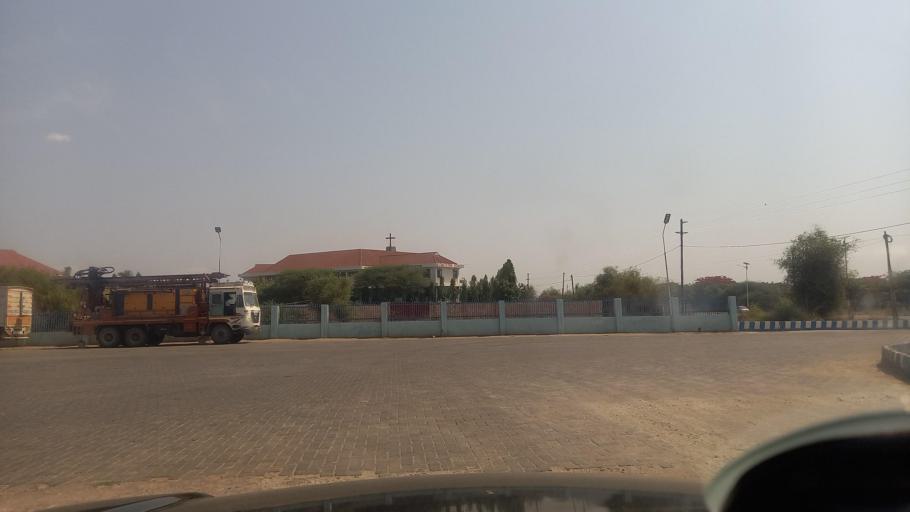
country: TZ
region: Dodoma
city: Kisasa
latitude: -6.1519
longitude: 35.8060
